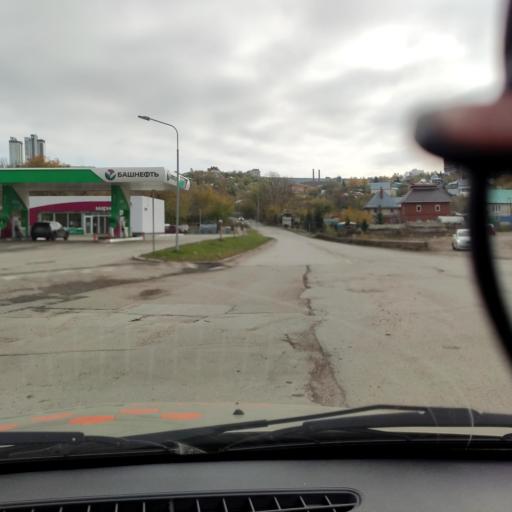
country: RU
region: Bashkortostan
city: Ufa
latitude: 54.7424
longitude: 55.9266
